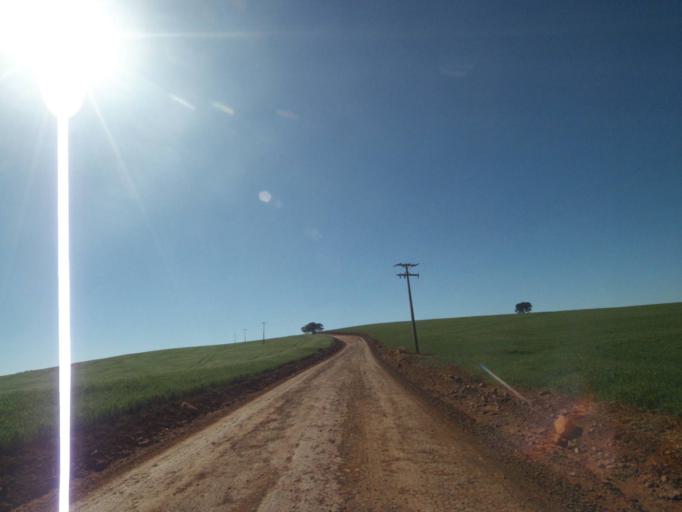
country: BR
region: Parana
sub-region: Tibagi
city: Tibagi
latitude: -24.6068
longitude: -50.6047
